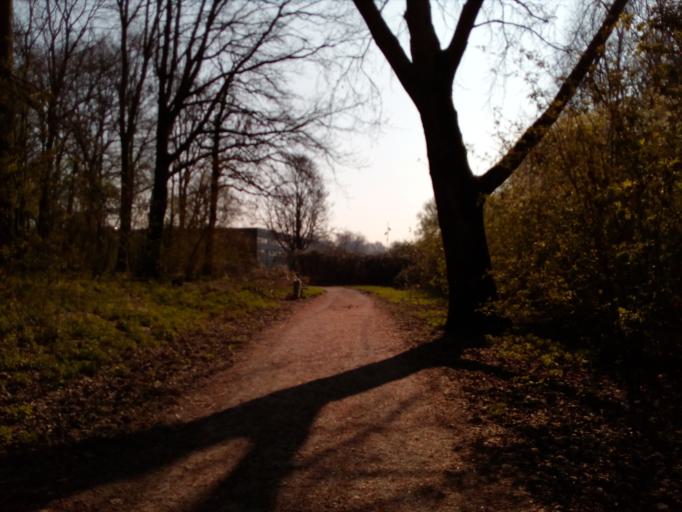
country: NL
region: South Holland
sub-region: Gemeente Zoetermeer
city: Zoetermeer
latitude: 52.0483
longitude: 4.5172
